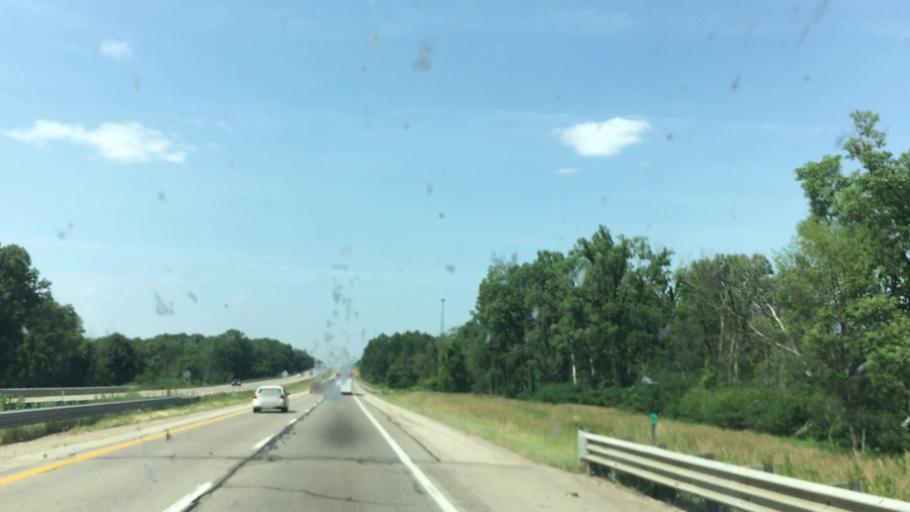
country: US
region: Michigan
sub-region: Allegan County
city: Wayland
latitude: 42.5665
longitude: -85.6622
